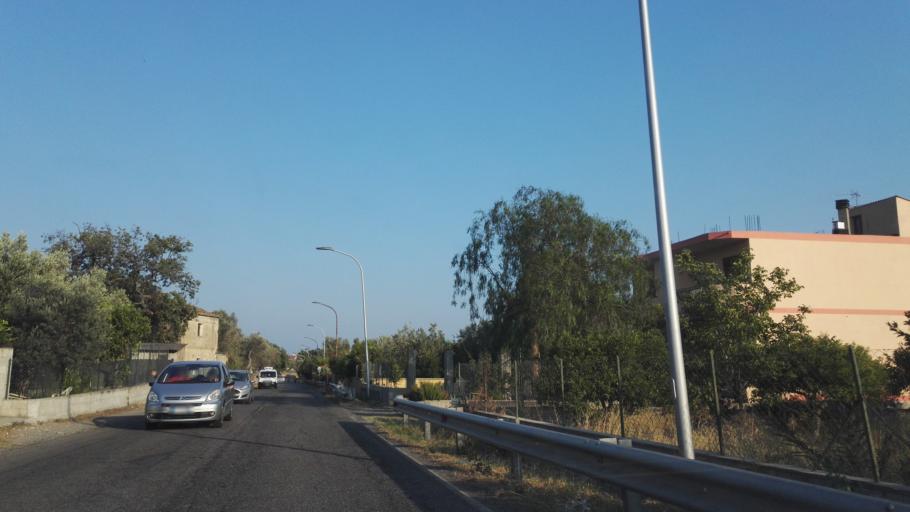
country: IT
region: Calabria
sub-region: Provincia di Reggio Calabria
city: Marina di Gioiosa Ionica
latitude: 38.3087
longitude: 16.3182
